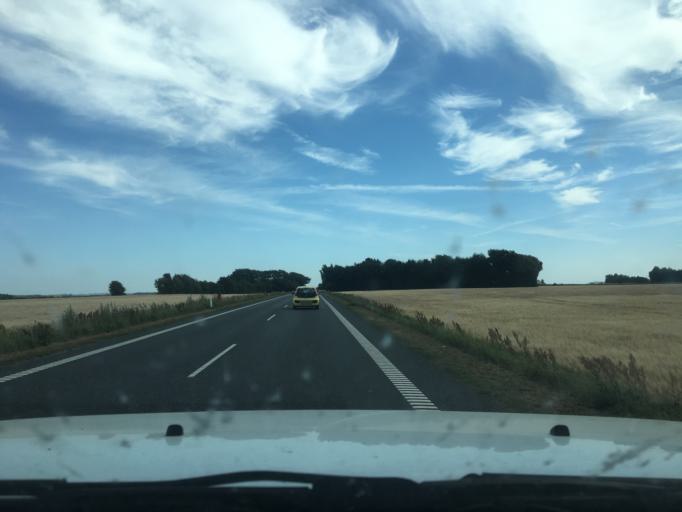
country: DK
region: Central Jutland
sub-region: Viborg Kommune
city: Viborg
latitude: 56.5929
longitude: 9.3650
